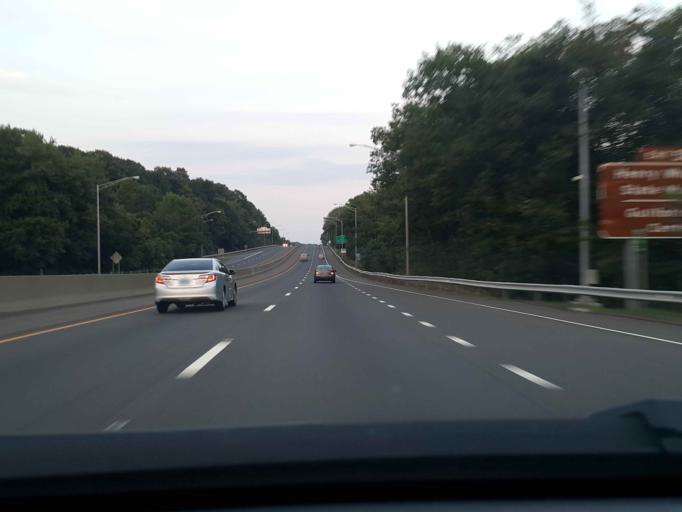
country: US
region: Connecticut
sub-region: New Haven County
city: Guilford
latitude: 41.2967
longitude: -72.7033
